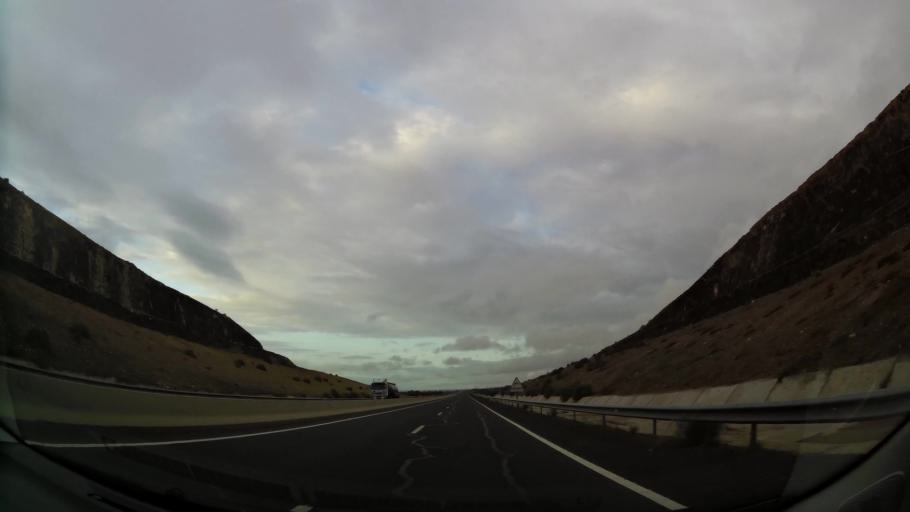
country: MA
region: Taza-Al Hoceima-Taounate
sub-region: Taza
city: Guercif
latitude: 34.3917
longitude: -3.2151
